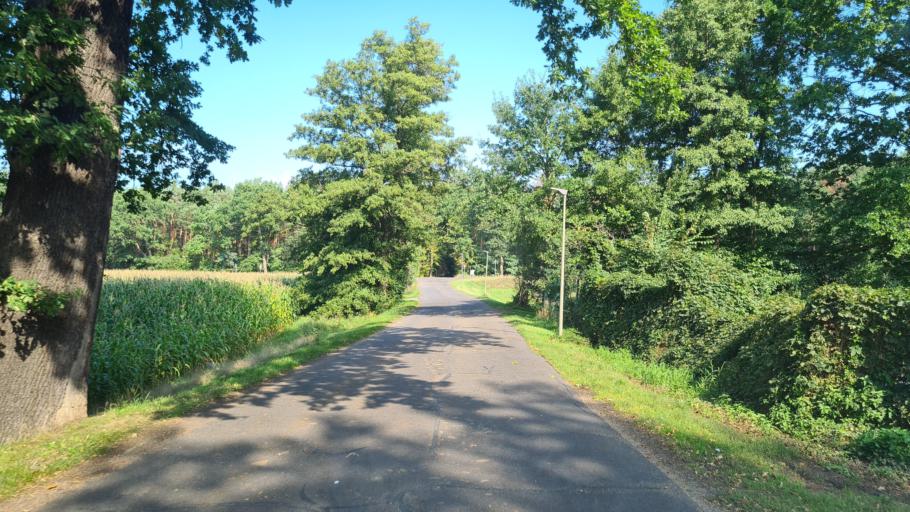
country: DE
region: Brandenburg
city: Kolkwitz
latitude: 51.7497
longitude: 14.2034
